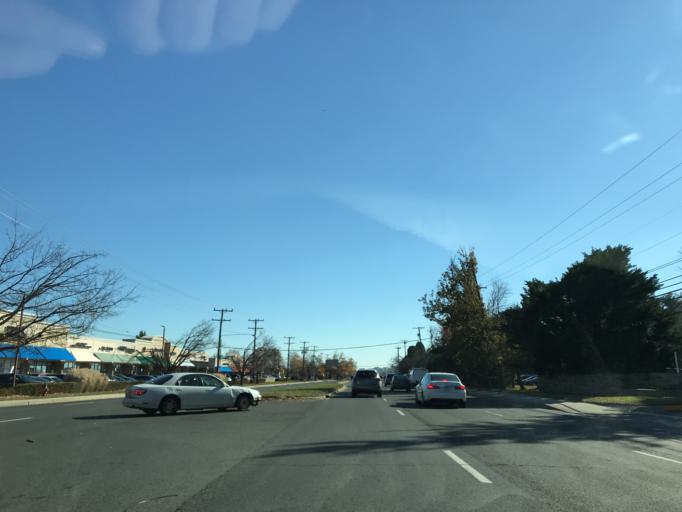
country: US
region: Maryland
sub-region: Montgomery County
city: Rockville
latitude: 39.0735
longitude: -77.1347
